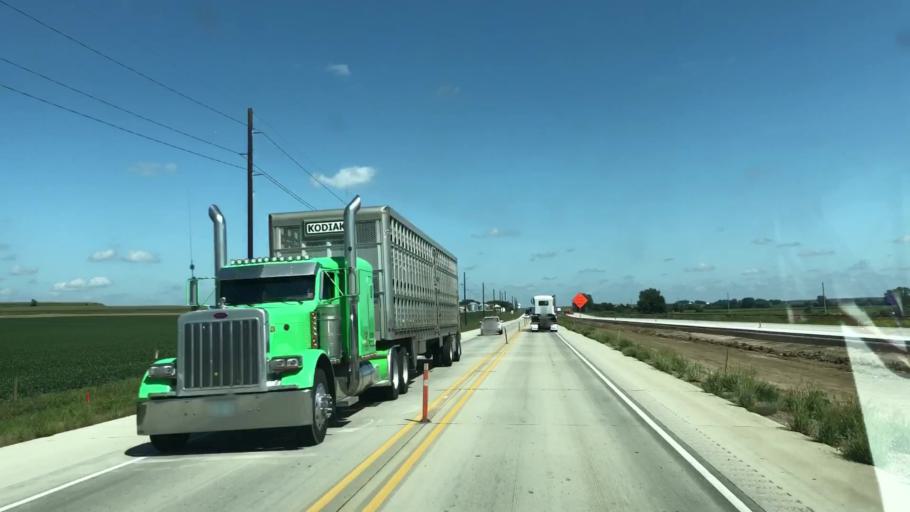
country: US
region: Iowa
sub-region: Plymouth County
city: Le Mars
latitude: 42.7302
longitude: -96.2315
